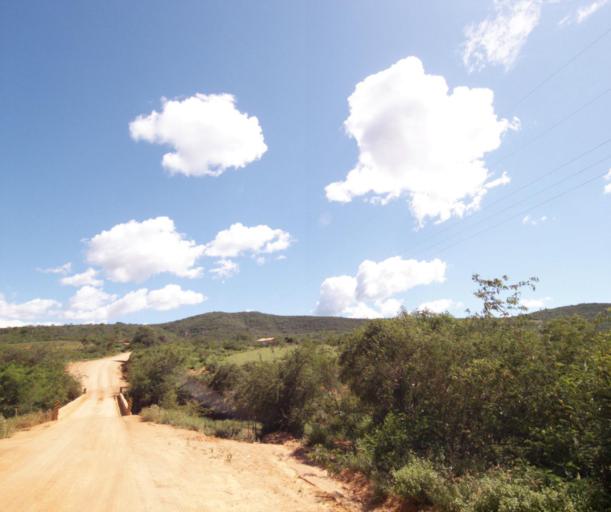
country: BR
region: Bahia
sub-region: Pocoes
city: Pocoes
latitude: -14.2715
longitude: -40.6940
